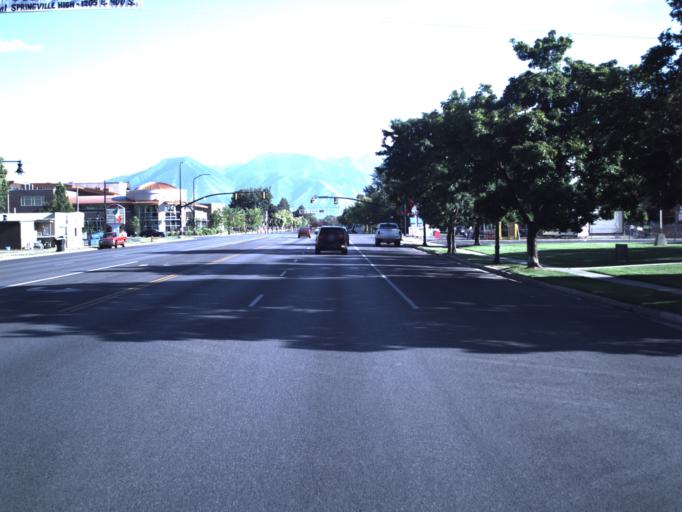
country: US
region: Utah
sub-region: Utah County
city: Springville
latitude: 40.1682
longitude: -111.6107
